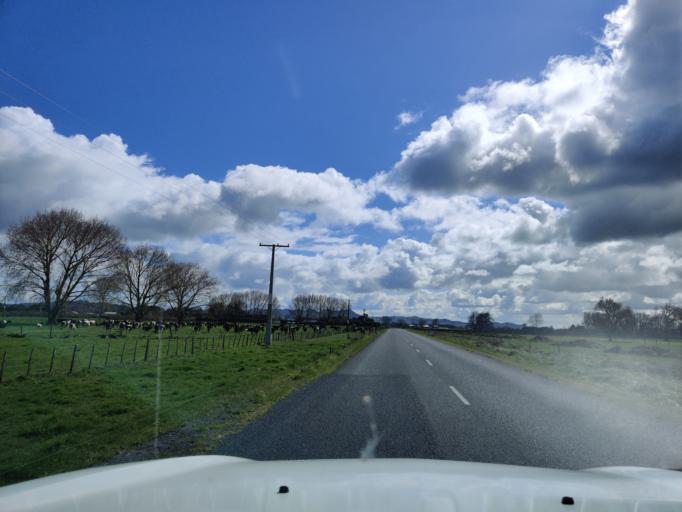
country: NZ
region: Waikato
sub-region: Waikato District
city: Ngaruawahia
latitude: -37.5906
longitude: 175.2905
